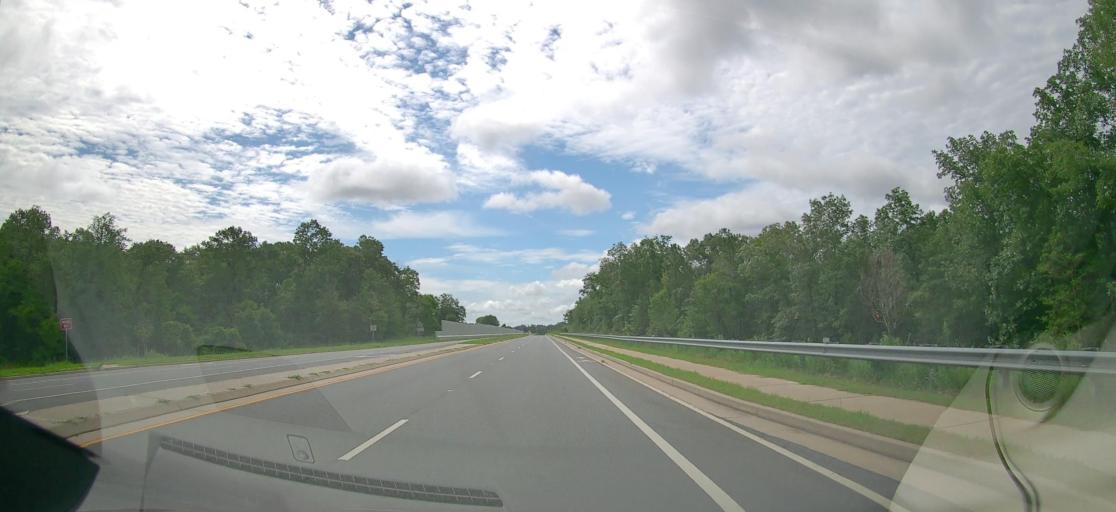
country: US
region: Georgia
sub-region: Peach County
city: Byron
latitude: 32.7159
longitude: -83.7033
